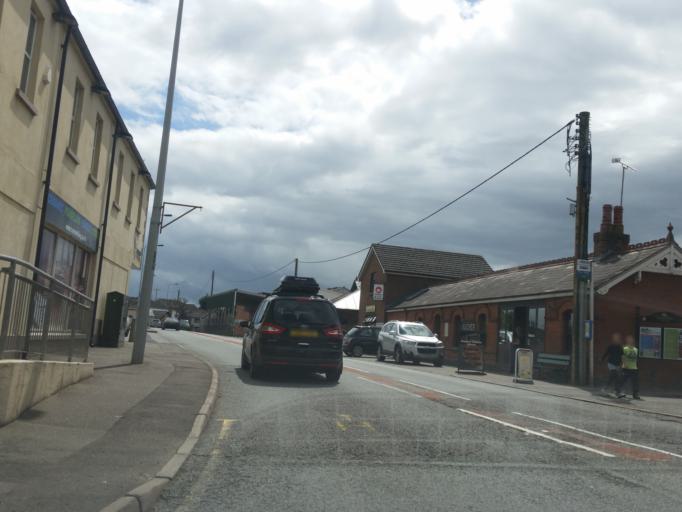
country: GB
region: Northern Ireland
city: Fivemiletown
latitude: 54.4287
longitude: -7.1320
